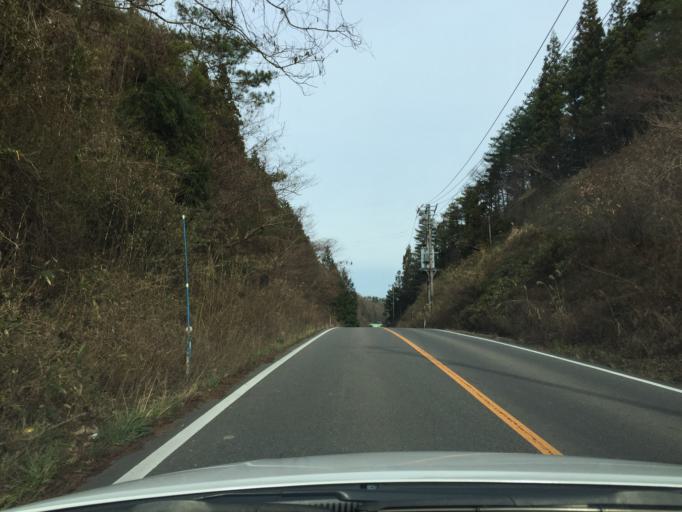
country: JP
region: Fukushima
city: Ishikawa
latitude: 37.2458
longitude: 140.6338
